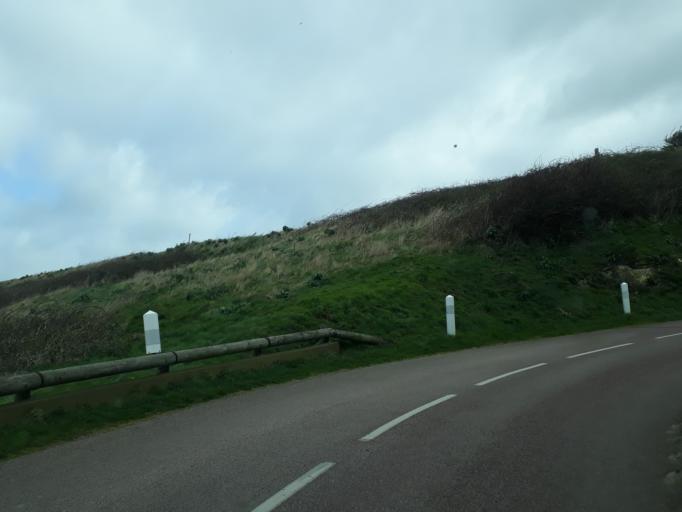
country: FR
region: Haute-Normandie
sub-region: Departement de la Seine-Maritime
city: Yport
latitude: 49.7385
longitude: 0.2934
